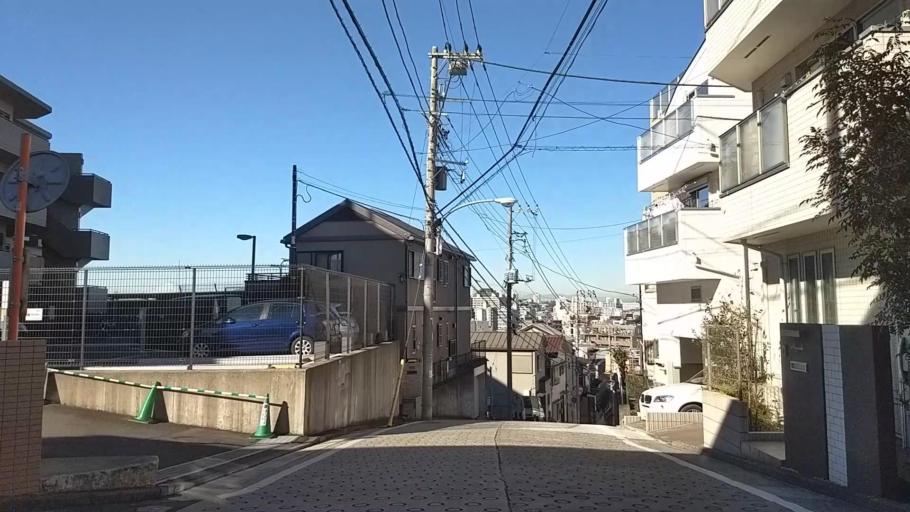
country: JP
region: Kanagawa
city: Yokohama
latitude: 35.4498
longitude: 139.6148
